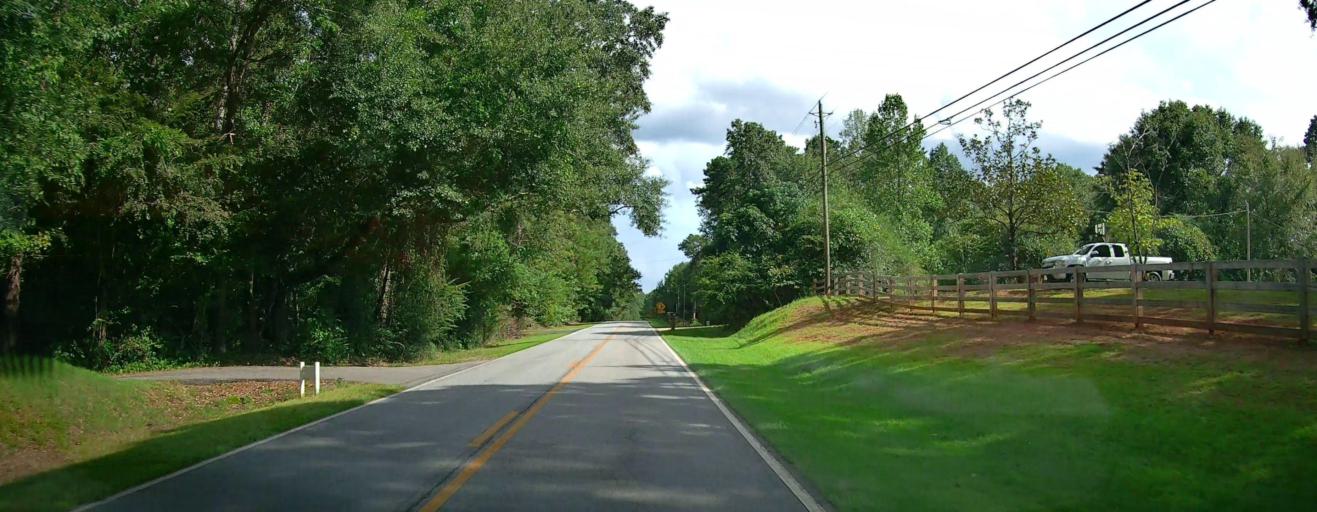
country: US
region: Alabama
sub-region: Russell County
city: Phenix City
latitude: 32.5837
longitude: -84.9759
